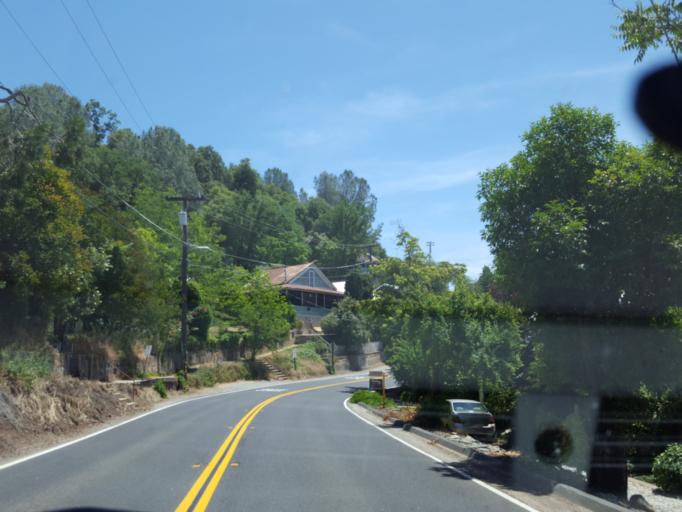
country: US
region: California
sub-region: Calaveras County
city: Angels Camp
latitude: 38.0663
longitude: -120.5378
